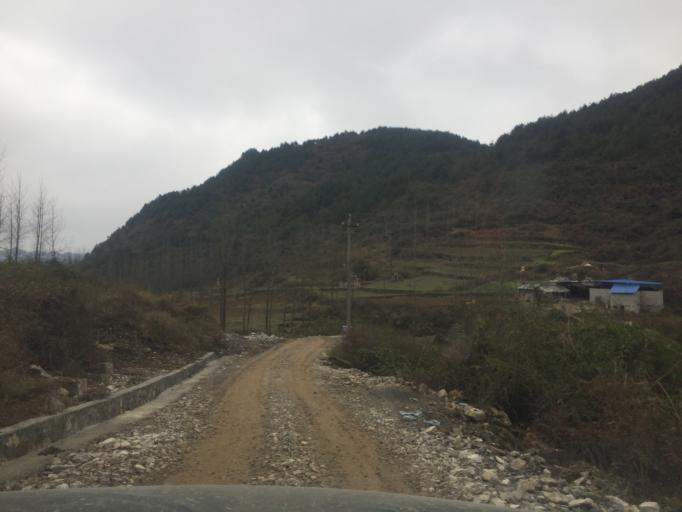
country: CN
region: Guizhou Sheng
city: Jiancha
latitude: 28.1751
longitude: 108.0017
